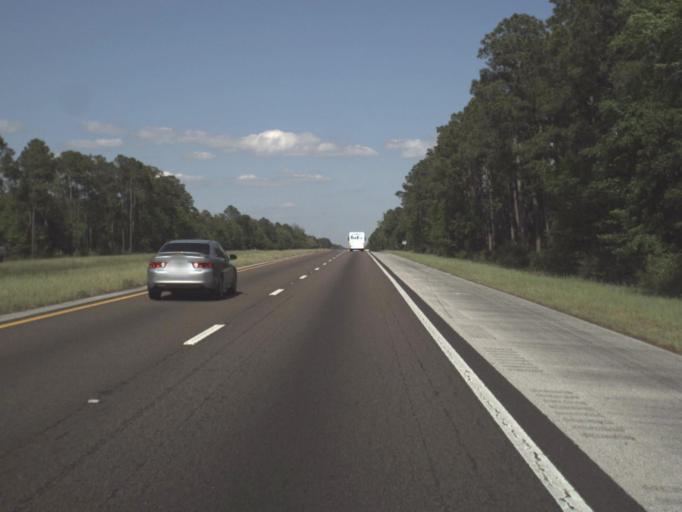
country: US
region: Florida
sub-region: Santa Rosa County
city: East Milton
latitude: 30.6321
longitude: -86.9272
